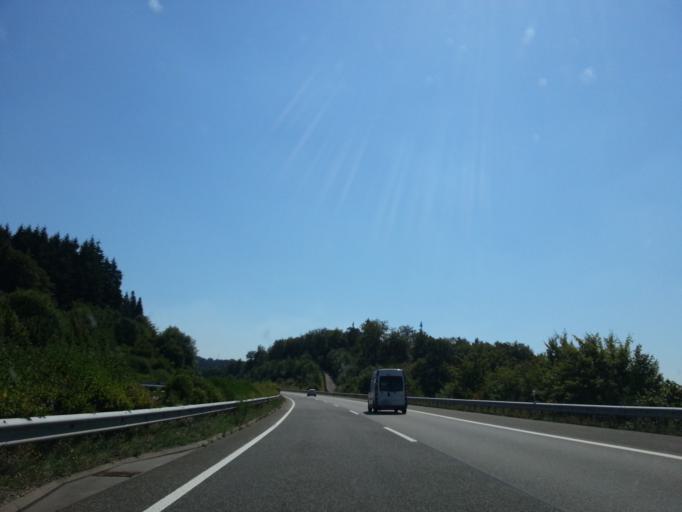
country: DE
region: Rheinland-Pfalz
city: Etteldorf
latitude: 50.0229
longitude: 6.5578
